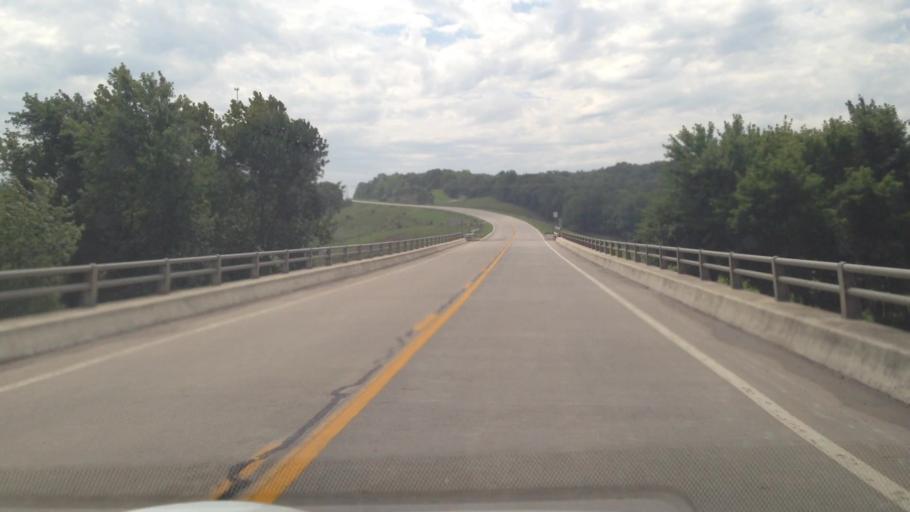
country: US
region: Kansas
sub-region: Bourbon County
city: Fort Scott
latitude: 37.8357
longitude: -94.9813
